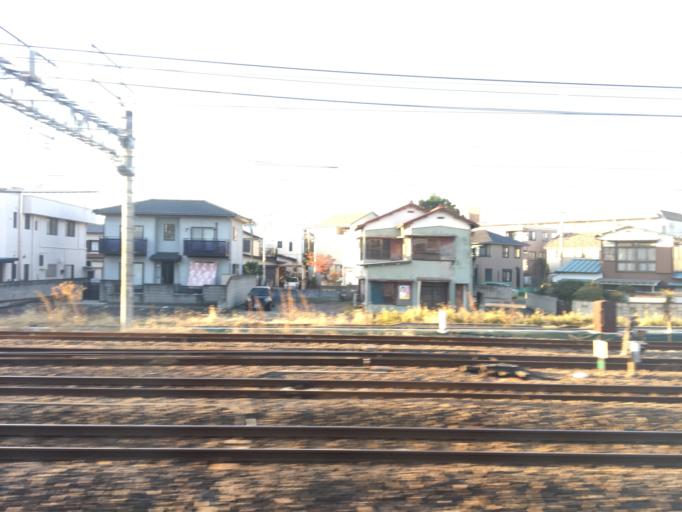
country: JP
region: Gunma
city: Maebashi-shi
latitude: 36.3815
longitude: 139.0503
